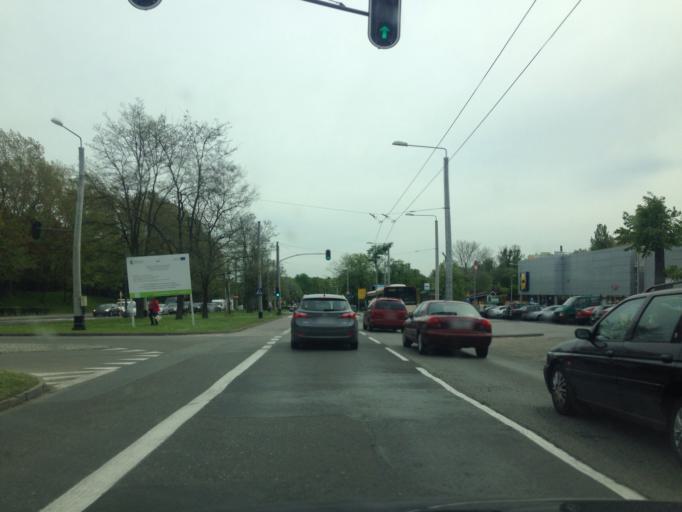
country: PL
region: Pomeranian Voivodeship
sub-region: Sopot
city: Sopot
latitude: 54.4590
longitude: 18.5544
